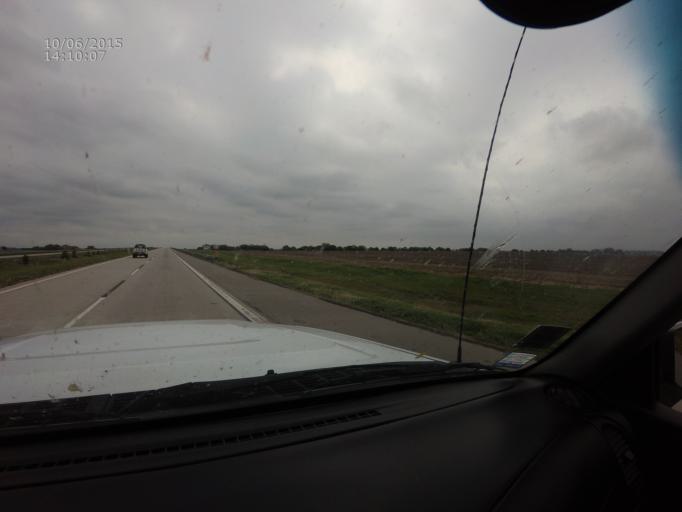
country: AR
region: Cordoba
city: Villa Maria
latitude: -32.4634
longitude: -63.0777
